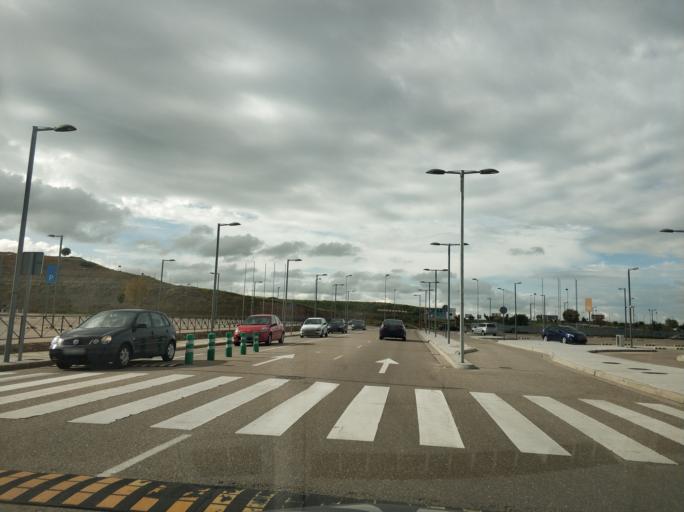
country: ES
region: Castille and Leon
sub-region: Provincia de Valladolid
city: Arroyo
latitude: 41.6300
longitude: -4.7867
